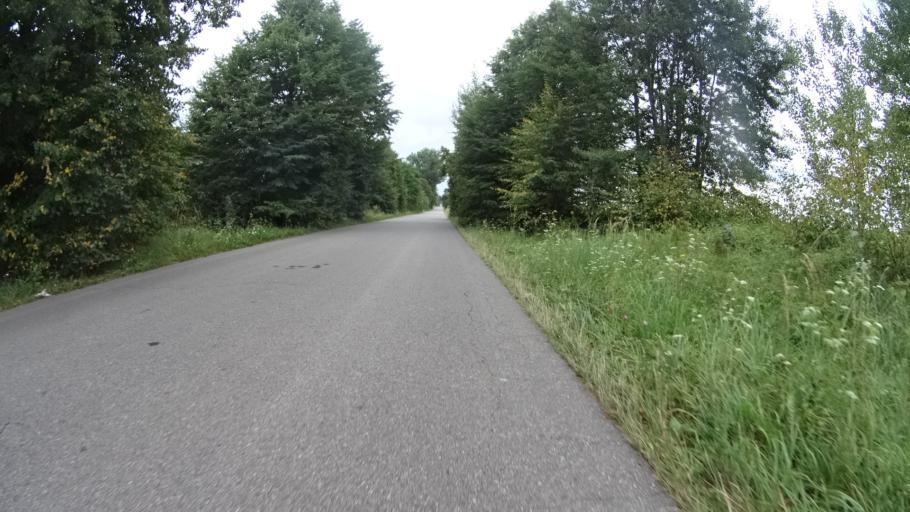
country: PL
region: Masovian Voivodeship
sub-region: Powiat grojecki
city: Goszczyn
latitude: 51.6780
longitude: 20.8594
